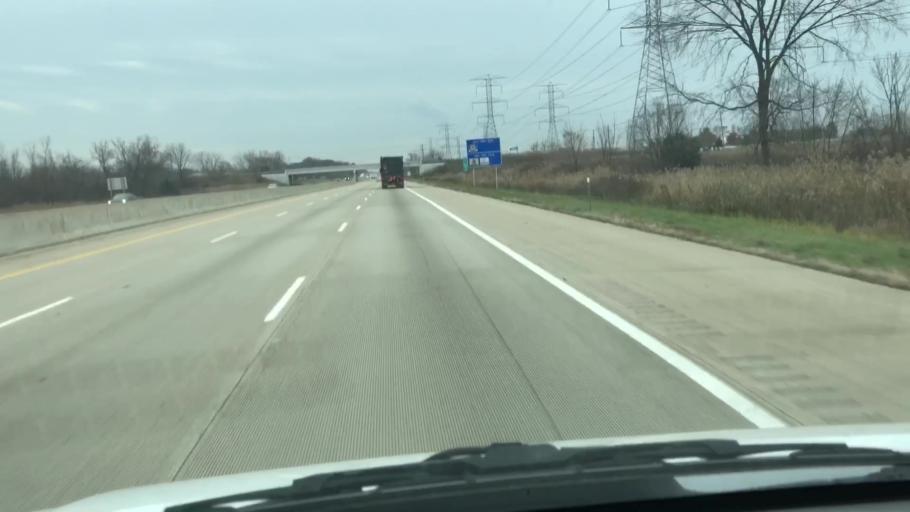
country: US
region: Michigan
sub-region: Wayne County
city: Woodhaven
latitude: 42.1124
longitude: -83.2417
